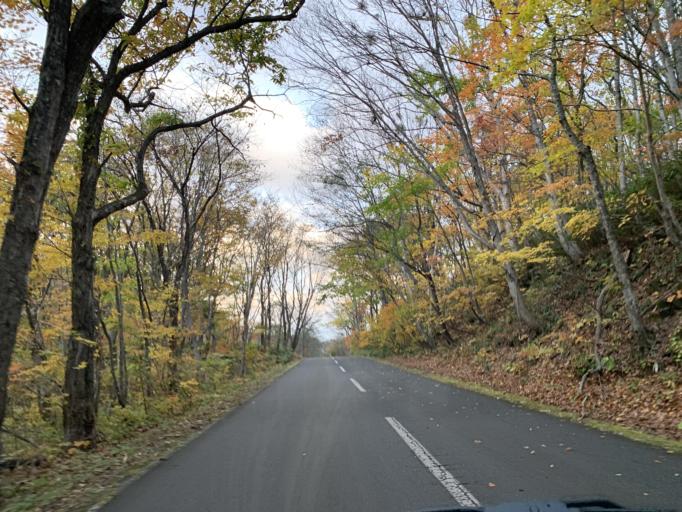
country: JP
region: Iwate
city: Mizusawa
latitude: 39.1148
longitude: 140.8811
